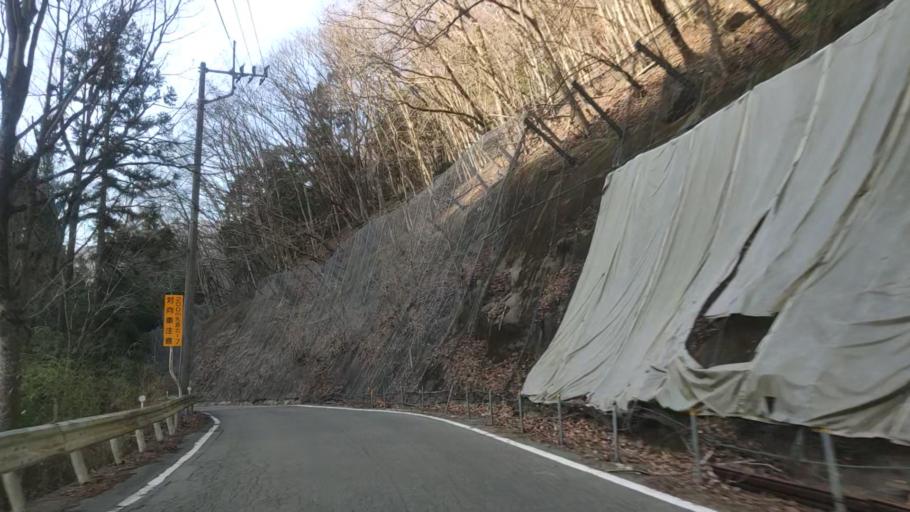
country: JP
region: Yamanashi
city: Fujikawaguchiko
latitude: 35.5365
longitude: 138.6247
